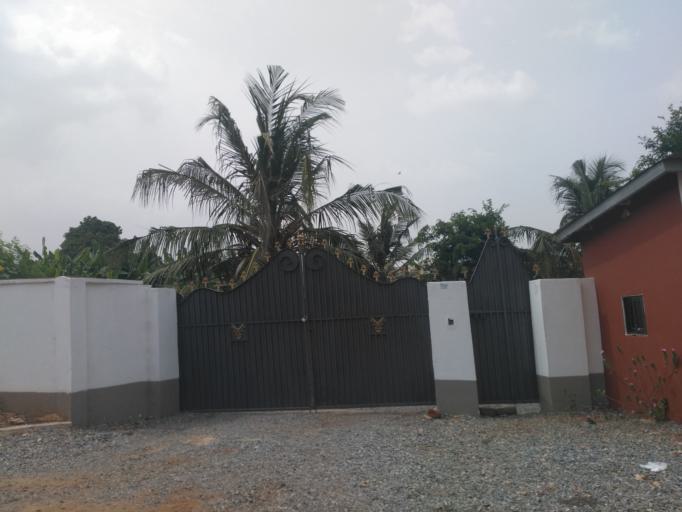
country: GH
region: Greater Accra
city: Accra
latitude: 5.5812
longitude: -0.1783
